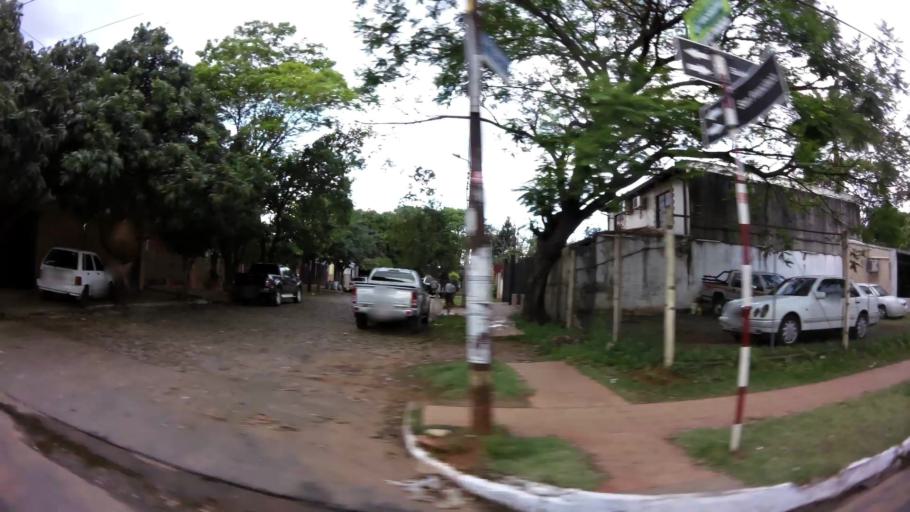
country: PY
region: Central
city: Lambare
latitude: -25.3321
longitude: -57.5652
